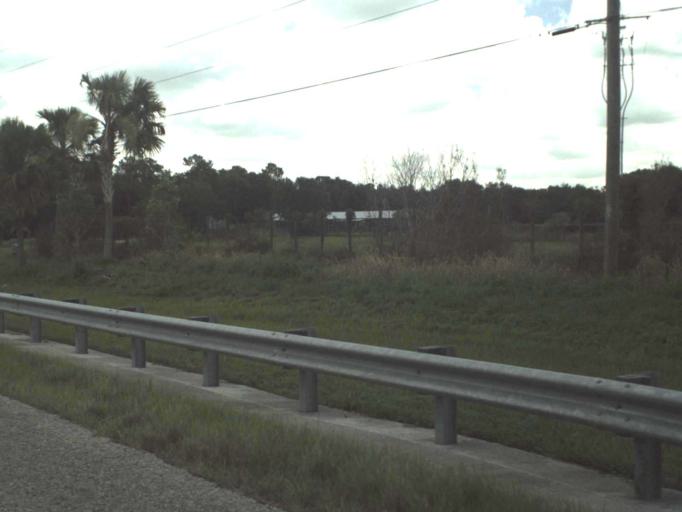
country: US
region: Florida
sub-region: Indian River County
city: Fellsmere
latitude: 27.6588
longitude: -80.7913
